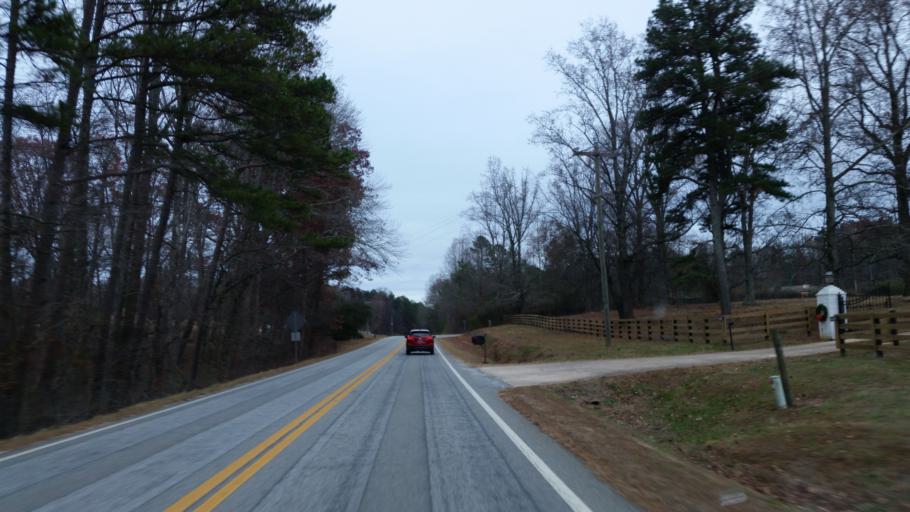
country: US
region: Georgia
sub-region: Dawson County
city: Dawsonville
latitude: 34.4403
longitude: -84.0854
